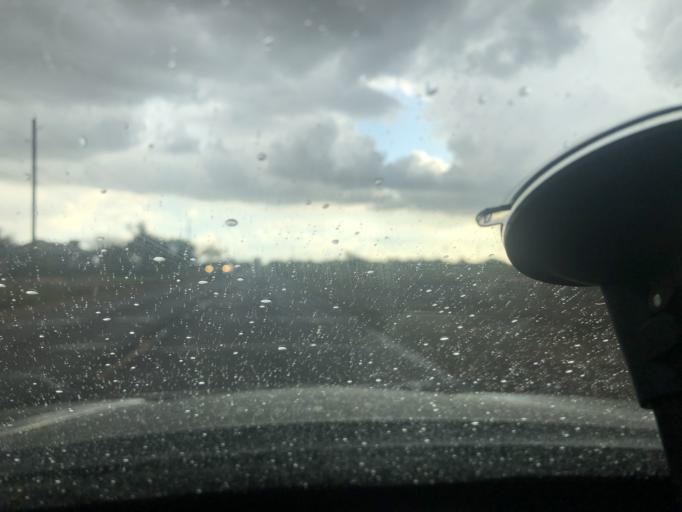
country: US
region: Arizona
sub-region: Maricopa County
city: Scottsdale
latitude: 33.4825
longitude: -111.8827
